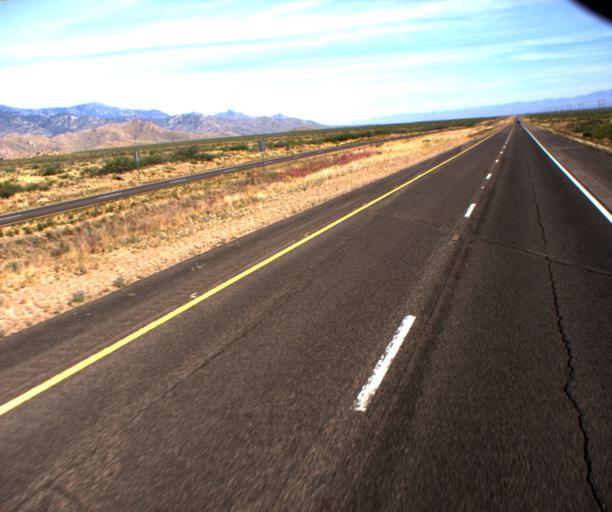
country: US
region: Arizona
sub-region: Graham County
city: Swift Trail Junction
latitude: 32.5391
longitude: -109.6756
